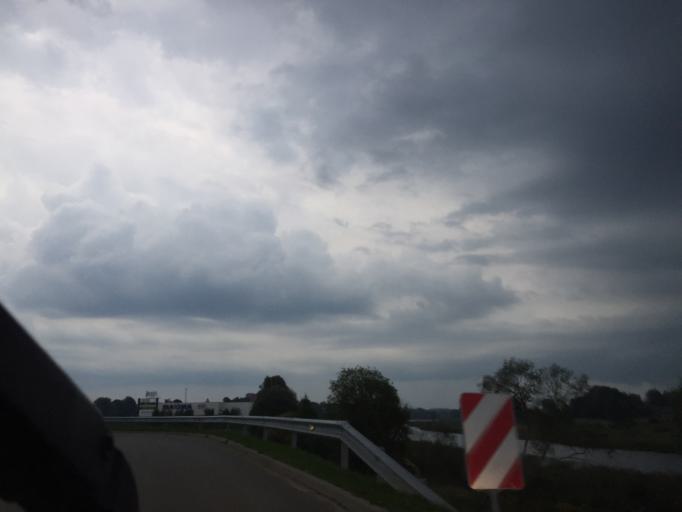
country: LV
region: Ogre
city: Ogre
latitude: 56.8170
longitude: 24.5789
